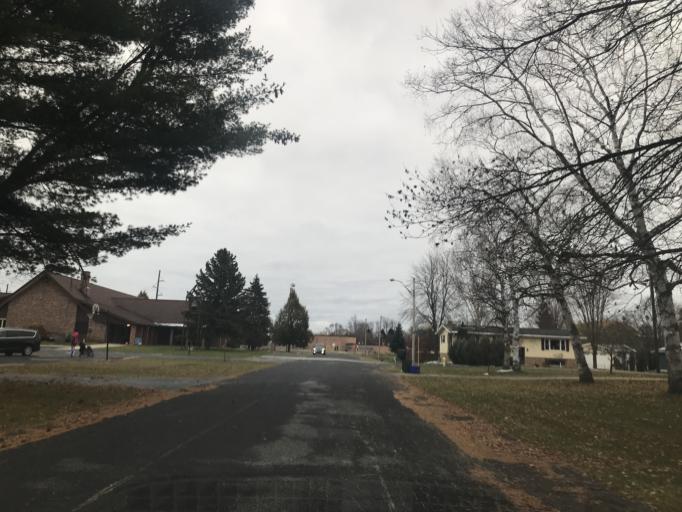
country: US
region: Wisconsin
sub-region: Marinette County
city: Marinette
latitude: 45.0956
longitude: -87.6529
